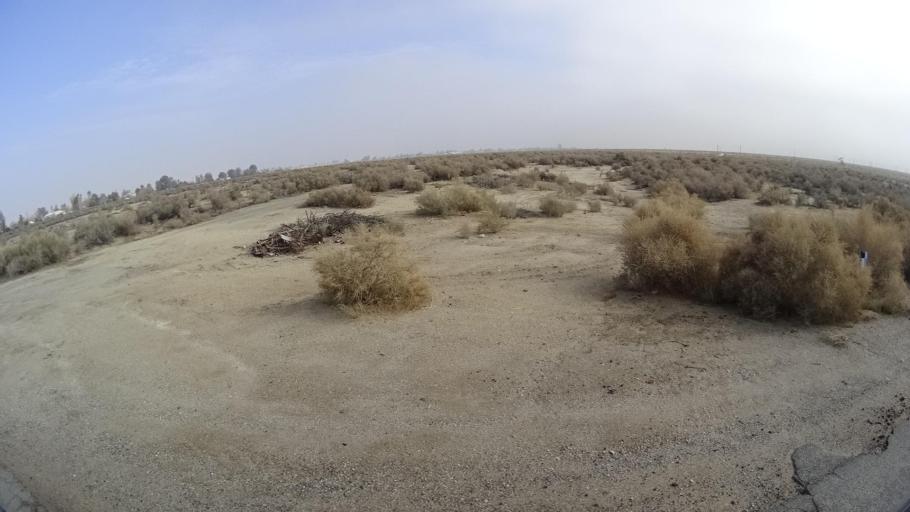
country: US
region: California
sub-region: Kern County
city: Ford City
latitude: 35.2069
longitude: -119.4297
